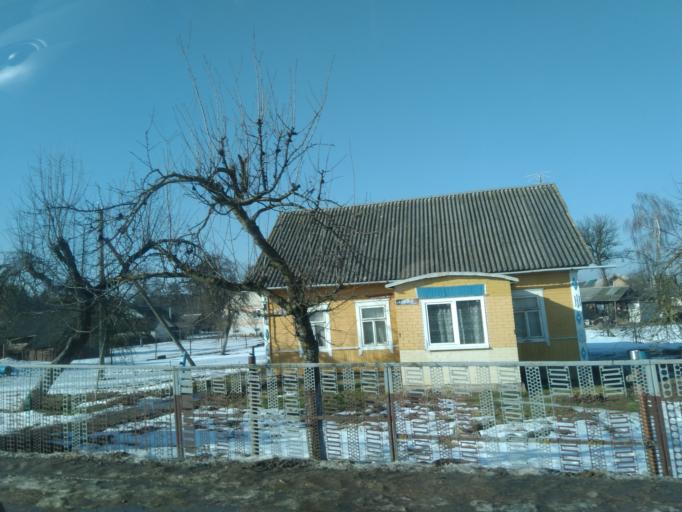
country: BY
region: Minsk
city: Nyasvizh
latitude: 53.2080
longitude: 26.6620
